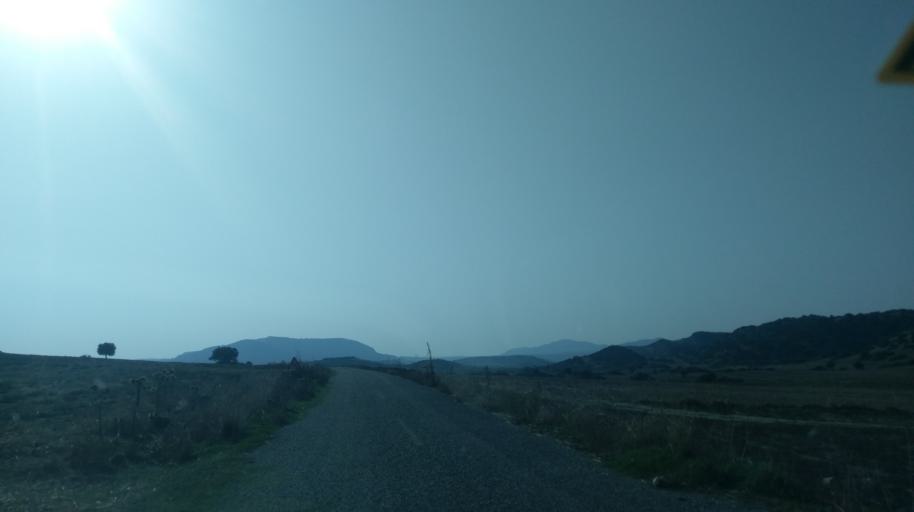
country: CY
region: Ammochostos
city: Rizokarpaso
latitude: 35.5499
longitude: 34.3514
